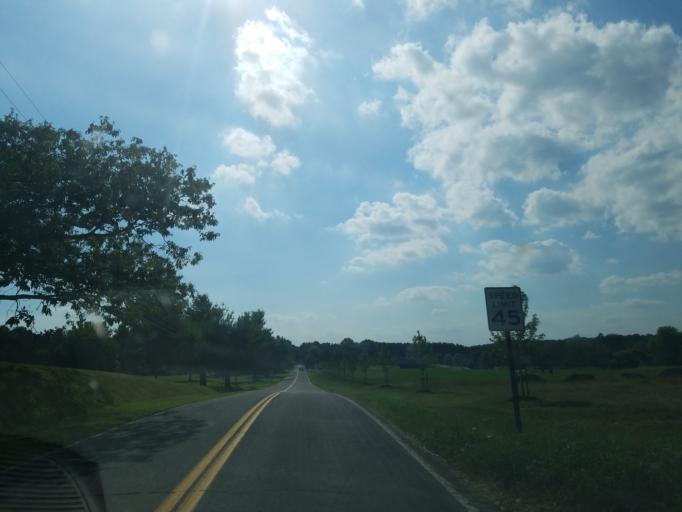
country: US
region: Ohio
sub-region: Portage County
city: Brimfield
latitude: 41.0505
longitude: -81.3203
